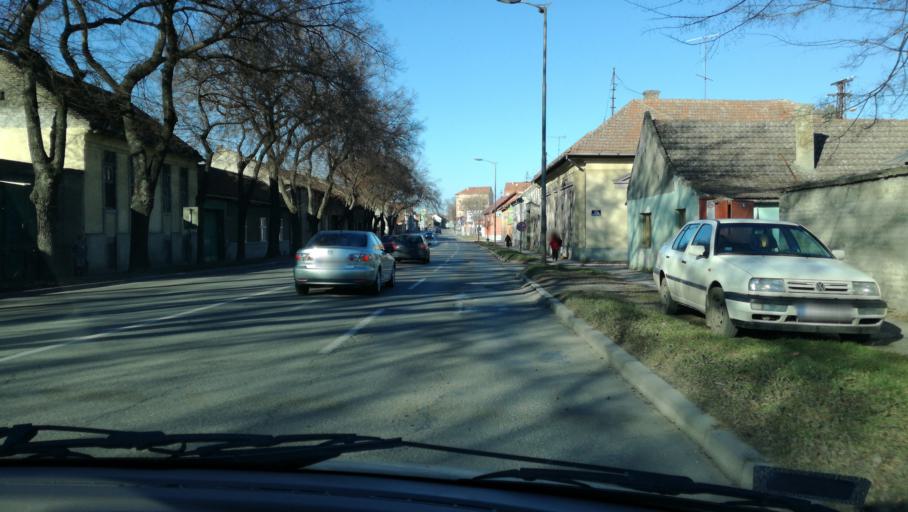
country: RS
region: Autonomna Pokrajina Vojvodina
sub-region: Severnobacki Okrug
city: Subotica
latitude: 46.0906
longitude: 19.6643
